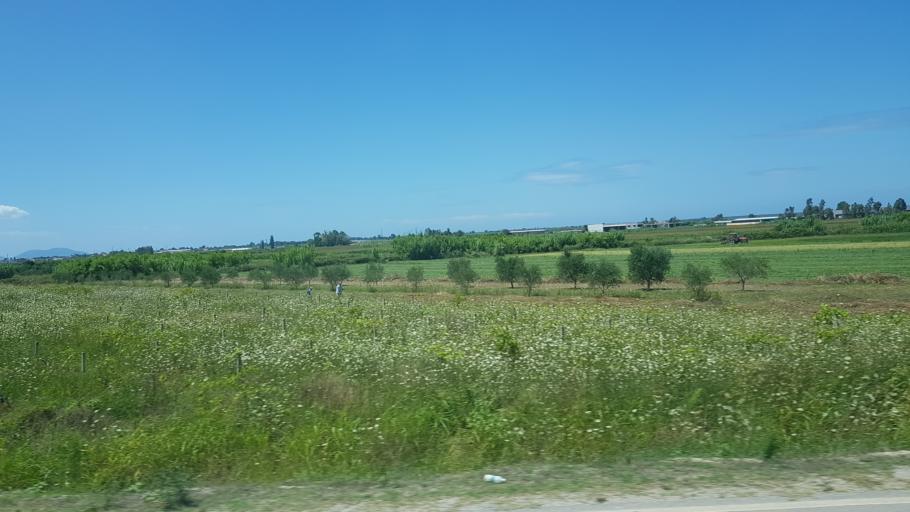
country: AL
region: Fier
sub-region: Rrethi i Fierit
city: Levan
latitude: 40.6651
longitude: 19.4878
